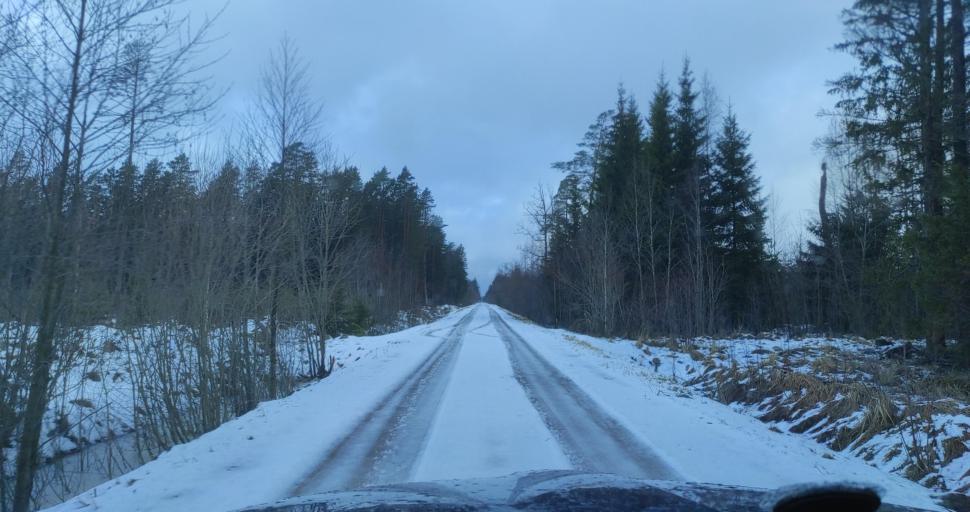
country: LV
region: Dundaga
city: Dundaga
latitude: 57.4069
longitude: 22.0917
